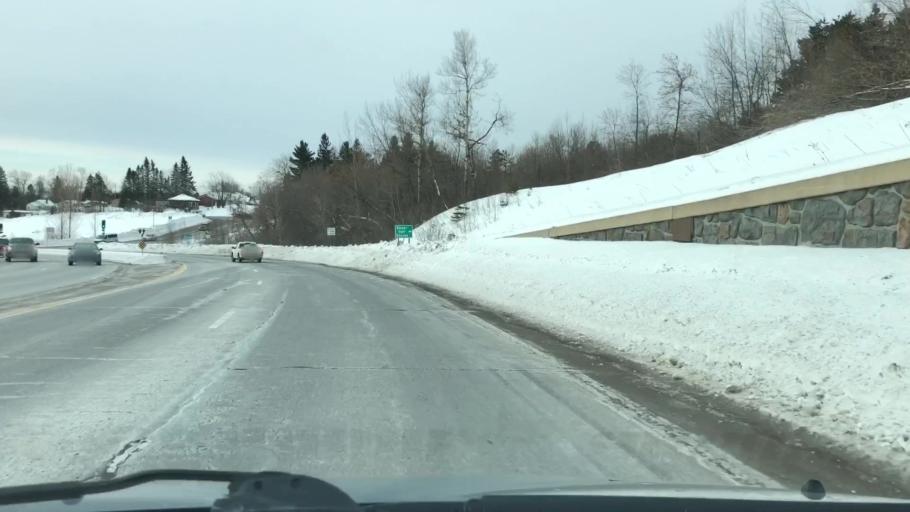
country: US
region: Minnesota
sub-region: Saint Louis County
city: Duluth
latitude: 46.7765
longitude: -92.1429
